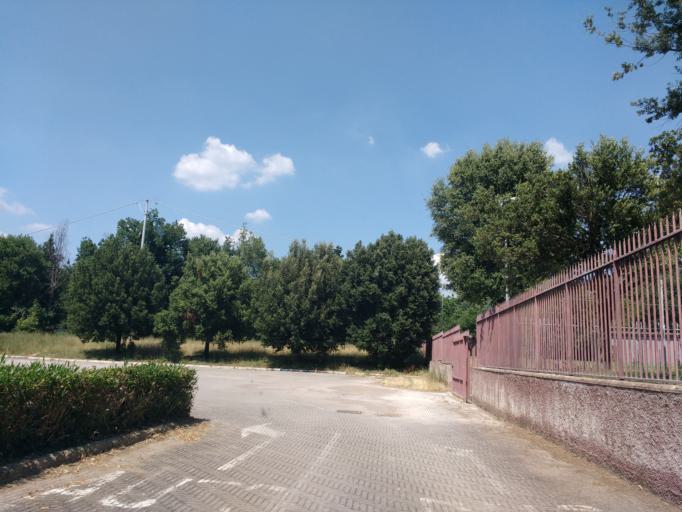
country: IT
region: Latium
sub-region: Citta metropolitana di Roma Capitale
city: Villa Adriana
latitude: 41.9465
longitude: 12.7741
